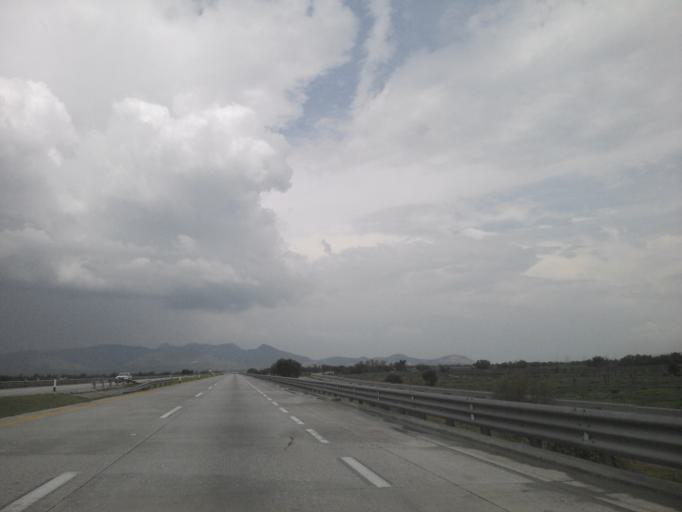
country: MX
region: Hidalgo
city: Doxey
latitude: 20.0863
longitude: -99.2568
